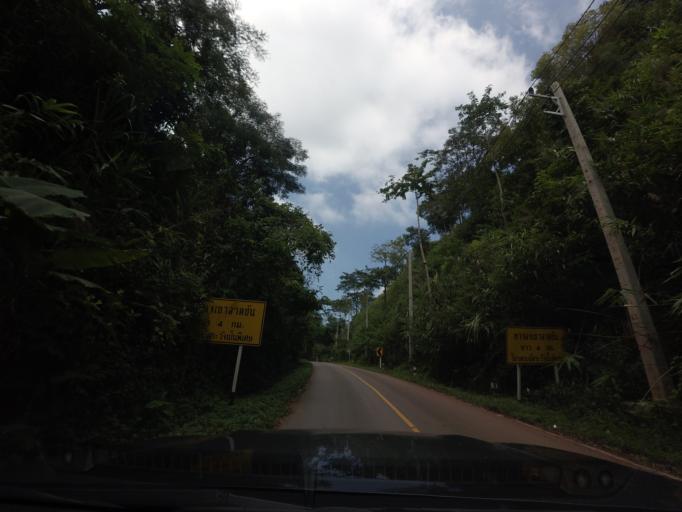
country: TH
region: Loei
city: Na Haeo
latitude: 17.4835
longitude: 100.9102
